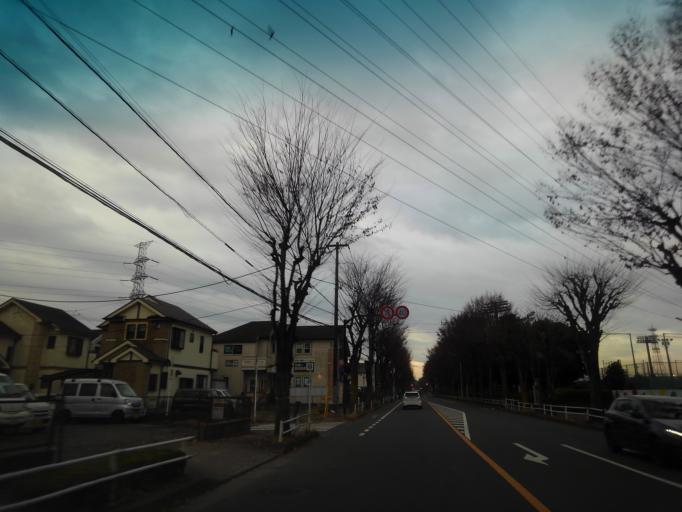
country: JP
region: Tokyo
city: Higashimurayama-shi
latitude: 35.7424
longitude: 139.4447
